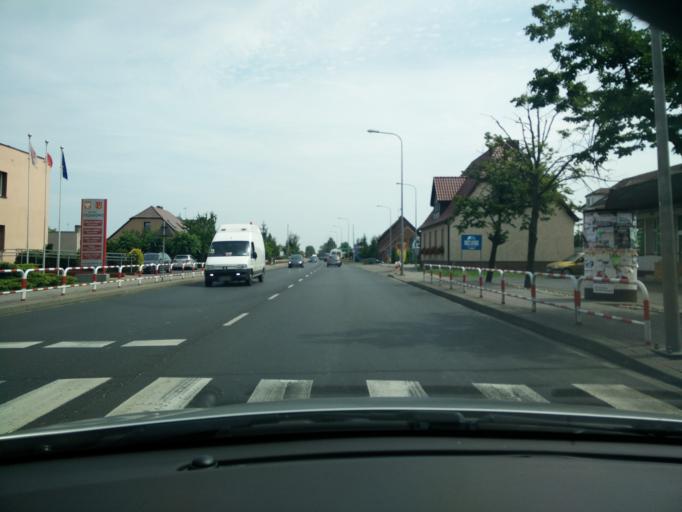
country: PL
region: Greater Poland Voivodeship
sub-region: Powiat slupecki
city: Strzalkowo
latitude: 52.3087
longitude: 17.8217
